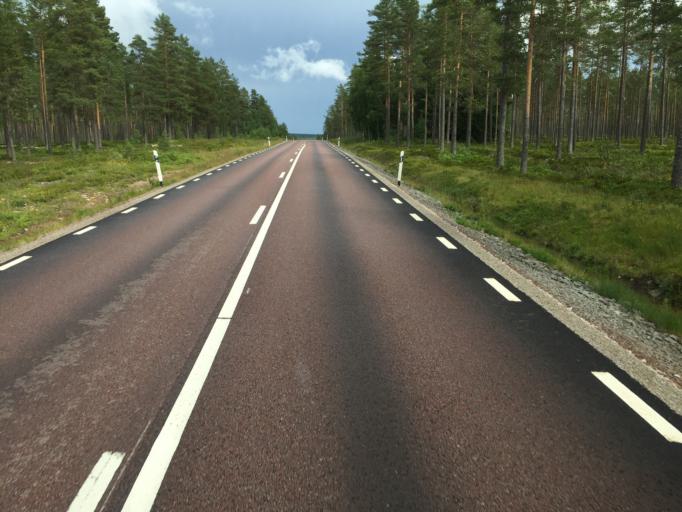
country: SE
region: Dalarna
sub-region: Malung-Saelens kommun
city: Malung
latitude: 60.8248
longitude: 14.0380
